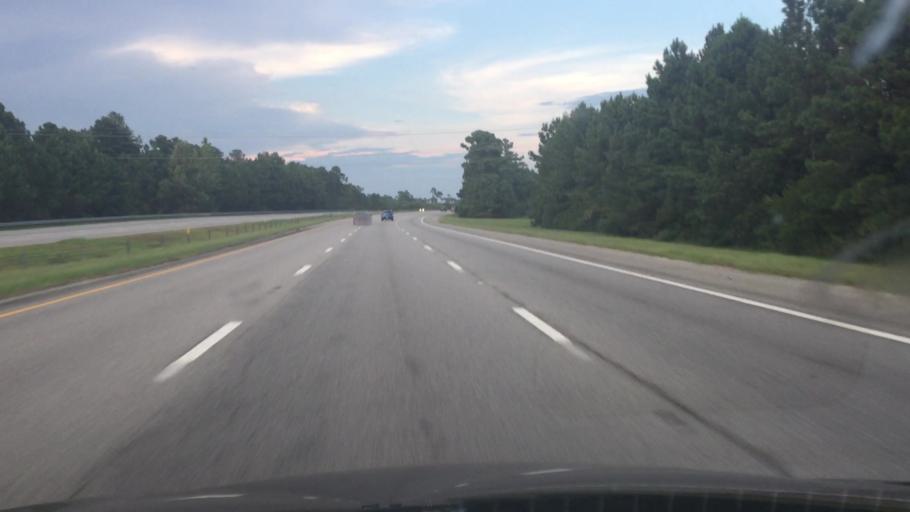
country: US
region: South Carolina
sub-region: Horry County
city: Myrtle Beach
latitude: 33.7641
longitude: -78.8351
